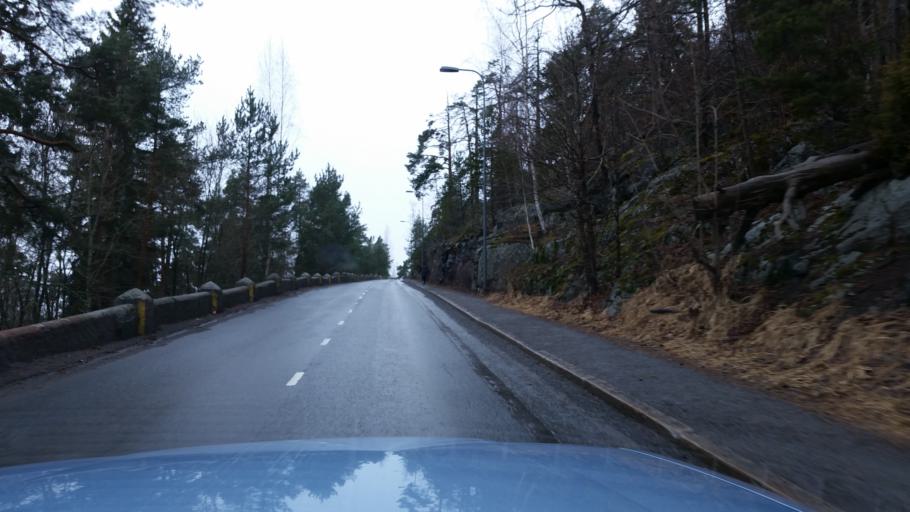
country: FI
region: Pirkanmaa
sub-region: Tampere
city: Tampere
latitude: 61.4942
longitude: 23.7198
